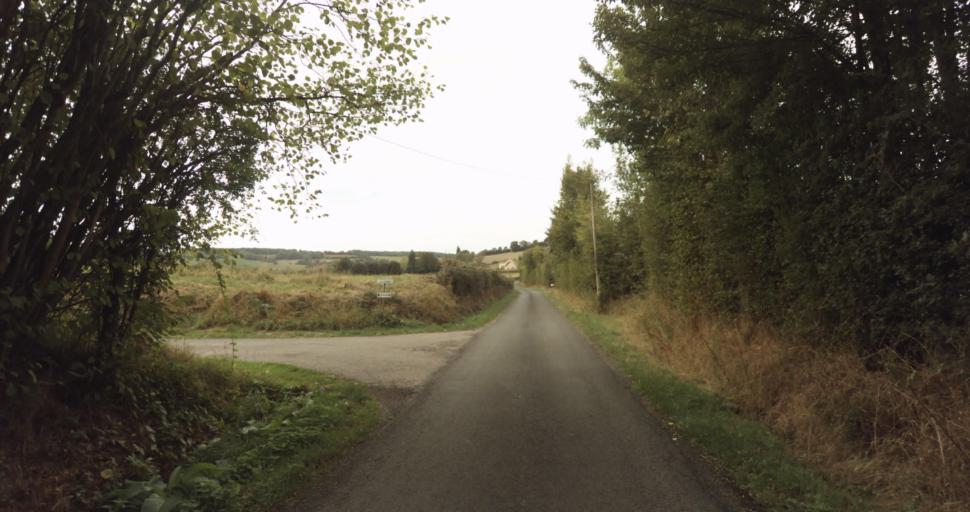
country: FR
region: Lower Normandy
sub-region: Departement de l'Orne
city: Gace
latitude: 48.8122
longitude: 0.2988
